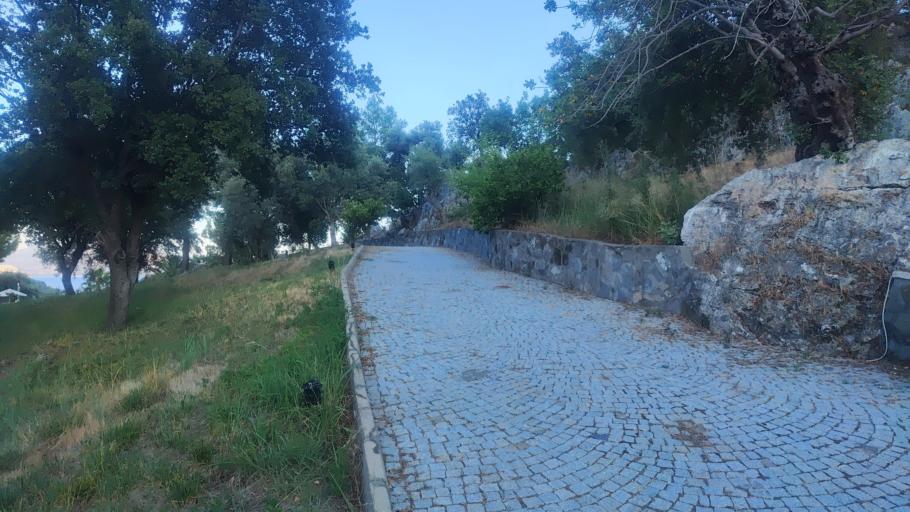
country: TR
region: Mugla
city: Sarigerme
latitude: 36.7056
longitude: 28.6940
